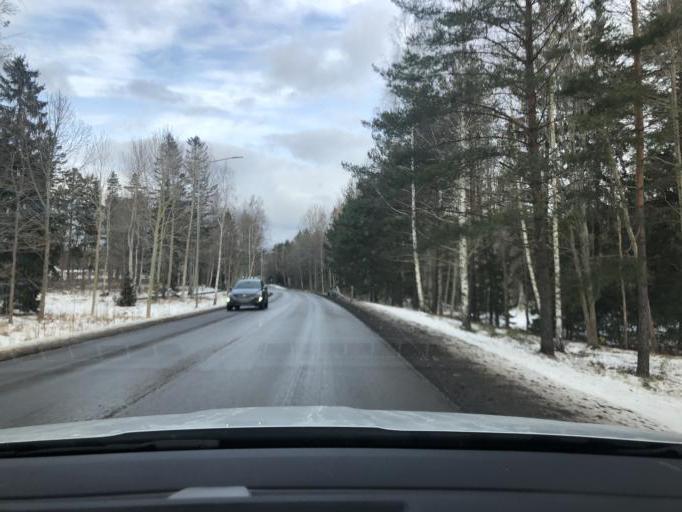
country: SE
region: OEstergoetland
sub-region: Motala Kommun
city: Motala
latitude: 58.5514
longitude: 15.0351
